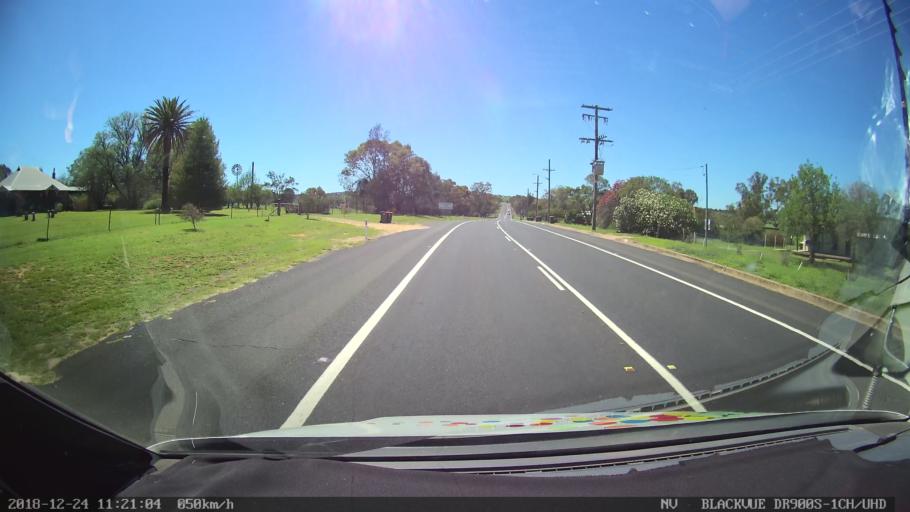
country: AU
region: New South Wales
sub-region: Upper Hunter Shire
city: Merriwa
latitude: -32.1415
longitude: 150.3675
